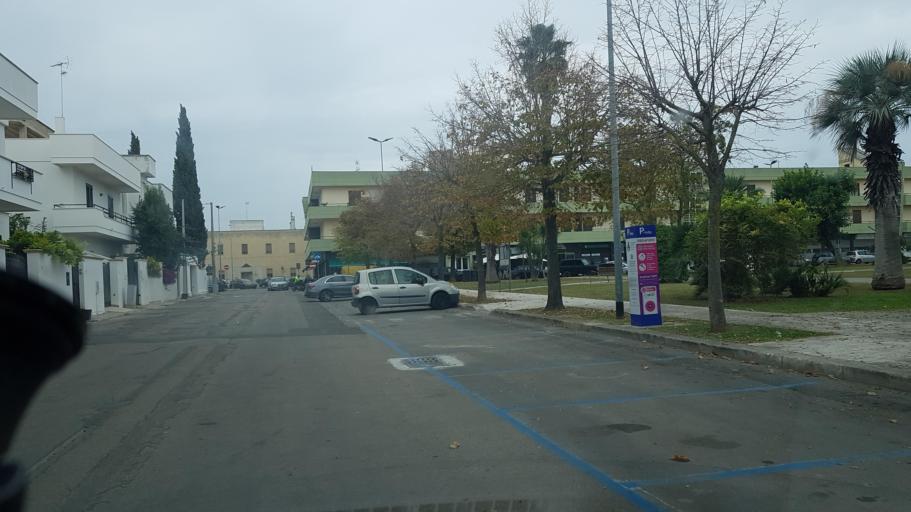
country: IT
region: Apulia
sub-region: Provincia di Lecce
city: Leverano
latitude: 40.2887
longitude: 17.9945
